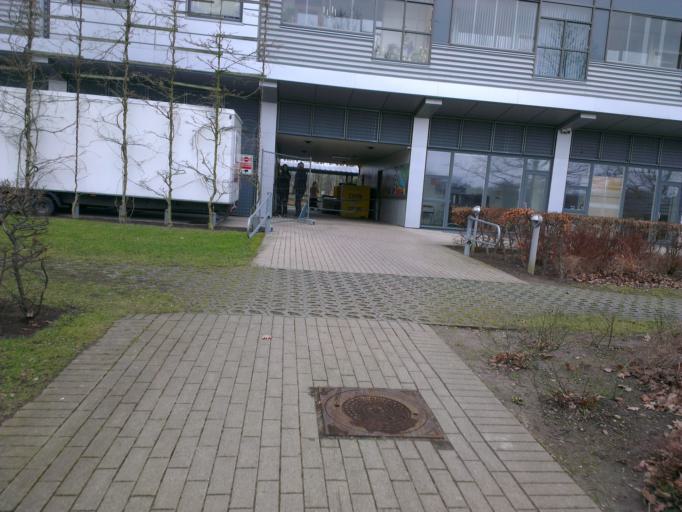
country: DK
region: Capital Region
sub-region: Frederikssund Kommune
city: Frederikssund
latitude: 55.8481
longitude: 12.0591
